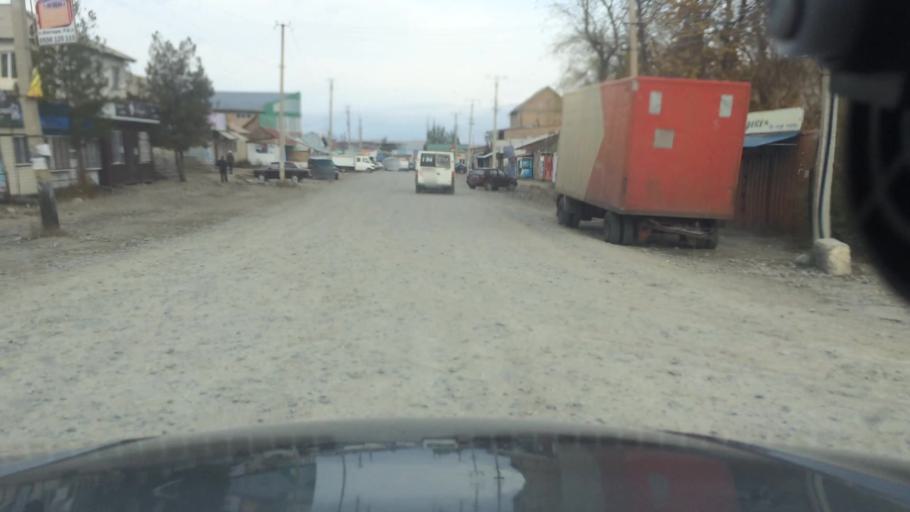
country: KG
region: Ysyk-Koel
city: Karakol
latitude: 42.4910
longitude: 78.3869
